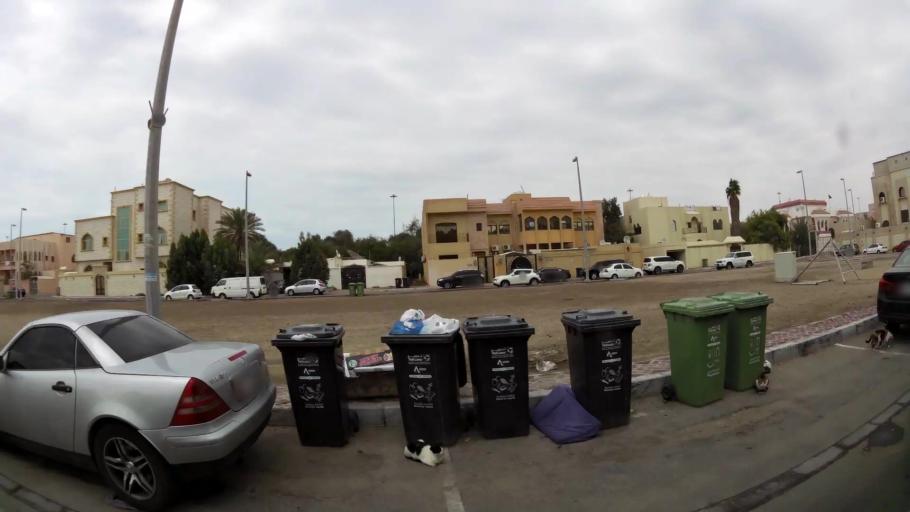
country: AE
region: Abu Dhabi
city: Abu Dhabi
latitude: 24.4341
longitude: 54.4058
